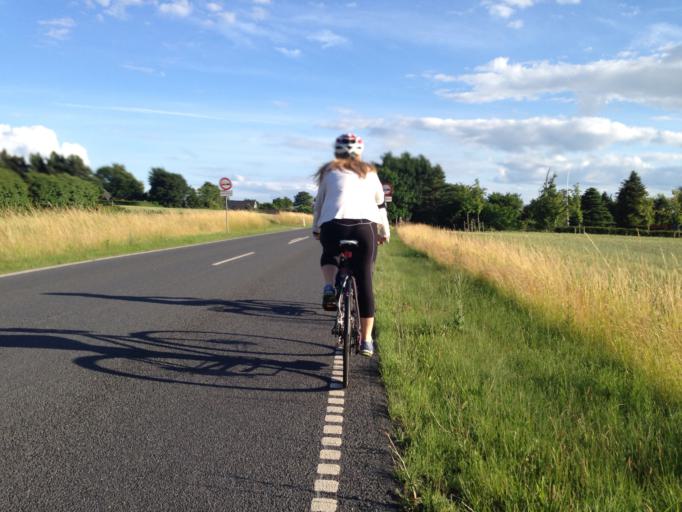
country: DK
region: South Denmark
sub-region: Middelfart Kommune
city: Norre Aby
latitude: 55.4838
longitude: 9.9021
